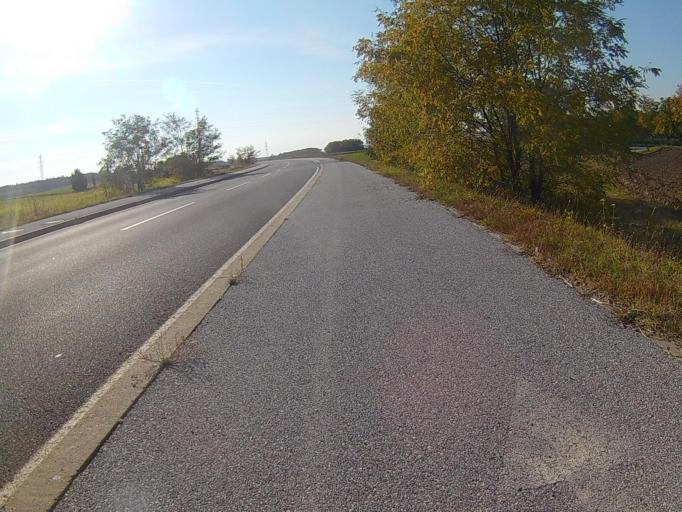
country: SI
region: Starse
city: Starse
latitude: 46.4466
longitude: 15.7898
